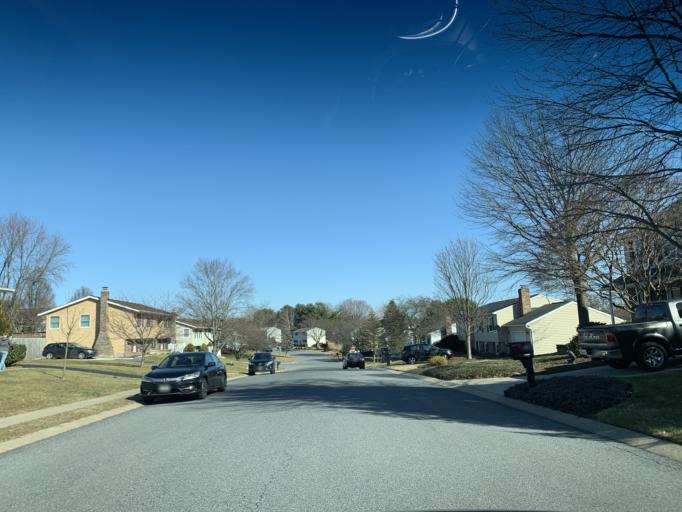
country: US
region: Maryland
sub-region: Carroll County
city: Westminster
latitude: 39.5952
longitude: -76.9930
